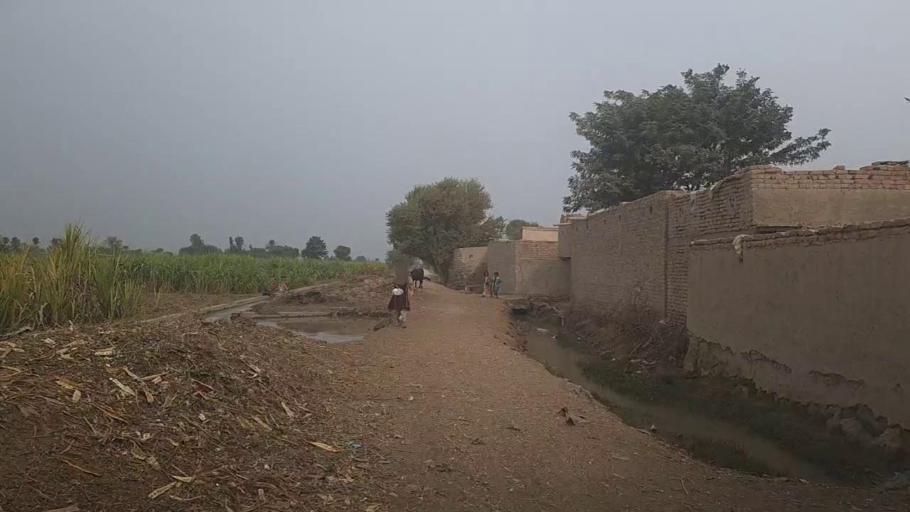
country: PK
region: Sindh
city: Gambat
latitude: 27.3031
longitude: 68.6059
